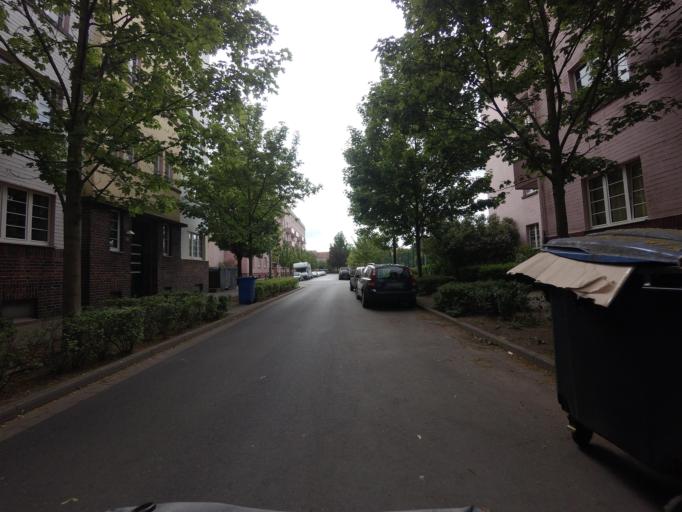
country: DE
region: Lower Saxony
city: Braunschweig
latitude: 52.2886
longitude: 10.5331
